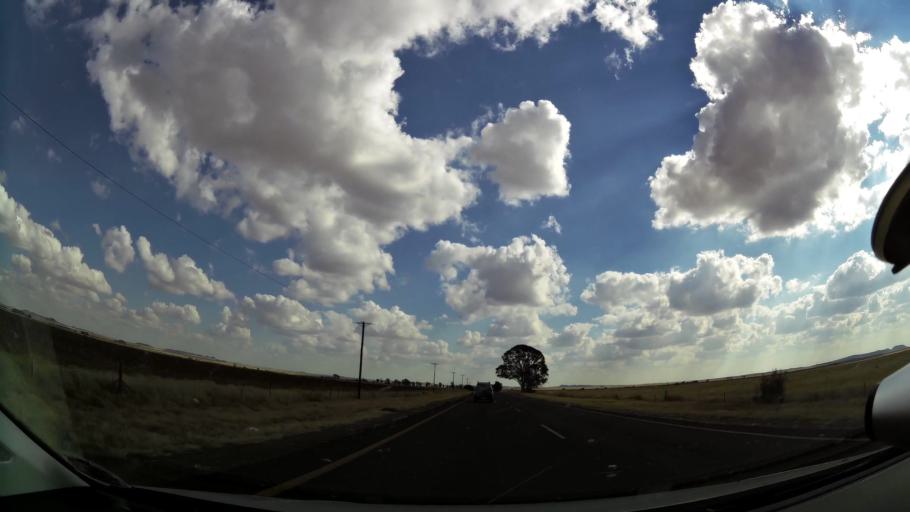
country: ZA
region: Orange Free State
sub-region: Xhariep District Municipality
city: Koffiefontein
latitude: -29.1324
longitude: 25.5406
